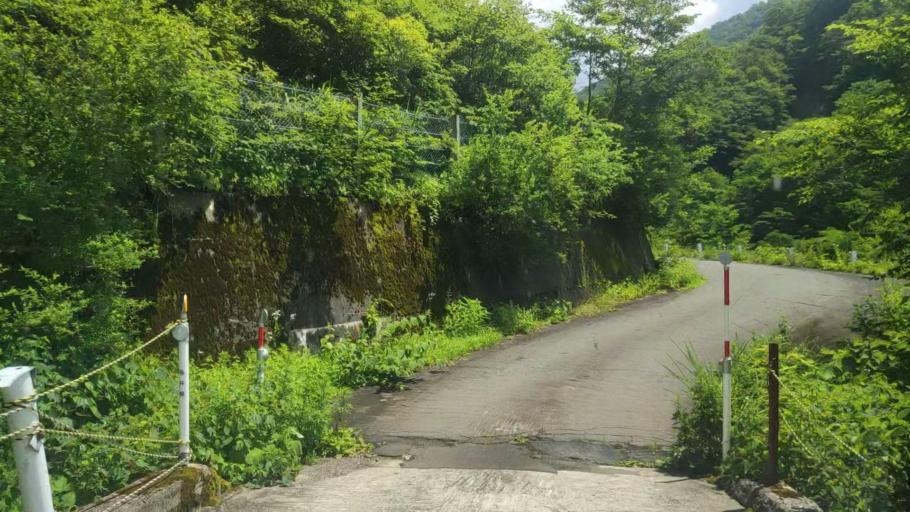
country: JP
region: Fukui
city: Ono
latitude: 35.7848
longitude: 136.5124
